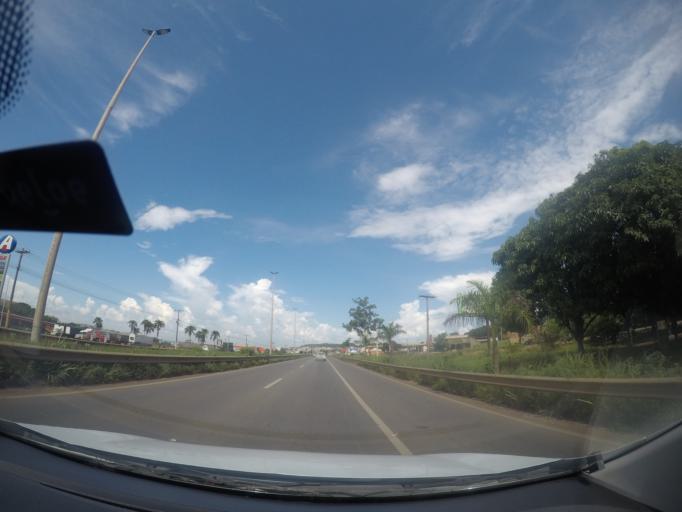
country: BR
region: Goias
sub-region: Trindade
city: Trindade
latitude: -16.6571
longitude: -49.3777
